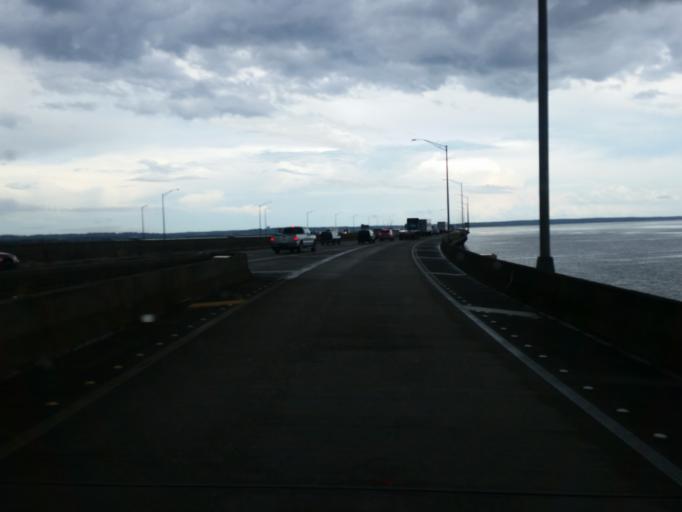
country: US
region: Alabama
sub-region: Mobile County
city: Mobile
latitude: 30.6765
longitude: -87.9857
